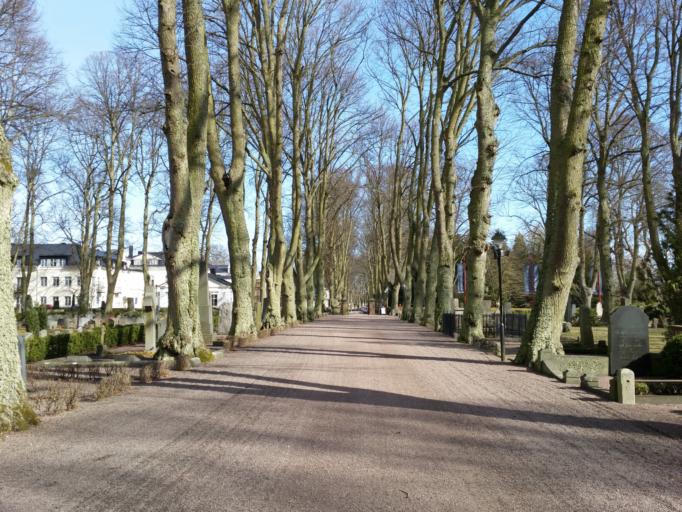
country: SE
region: Kalmar
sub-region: Kalmar Kommun
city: Kalmar
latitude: 56.6582
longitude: 16.3519
